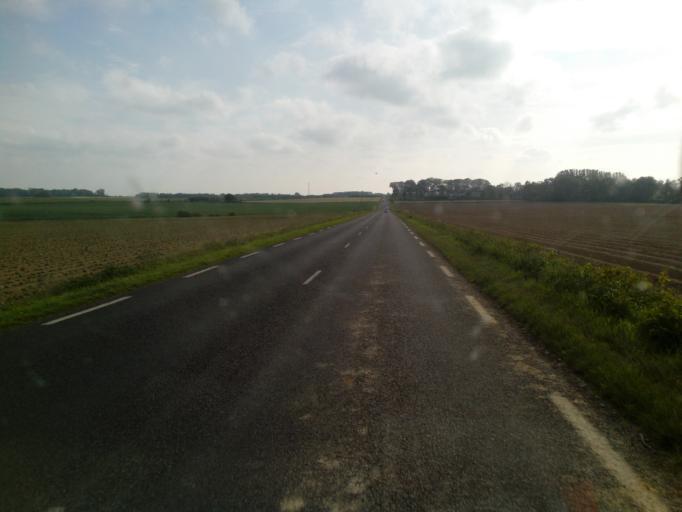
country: FR
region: Haute-Normandie
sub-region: Departement de la Seine-Maritime
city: Sainte-Marie-des-Champs
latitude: 49.6403
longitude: 0.8296
